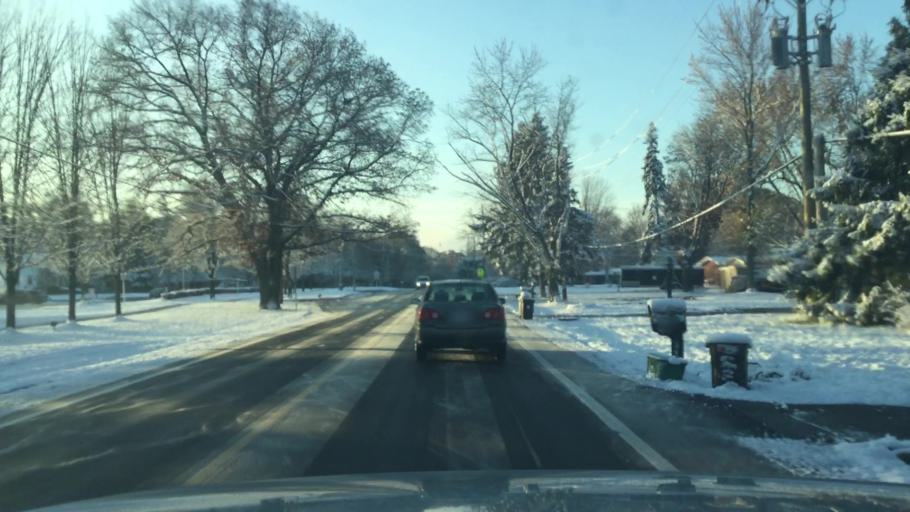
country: US
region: Michigan
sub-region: Oakland County
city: Wolverine Lake
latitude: 42.5533
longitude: -83.4786
